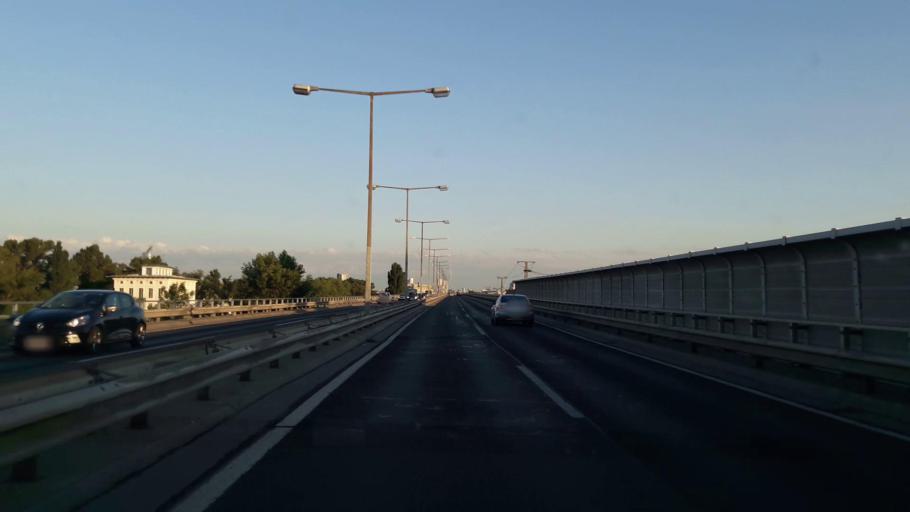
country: AT
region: Lower Austria
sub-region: Politischer Bezirk Korneuburg
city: Langenzersdorf
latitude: 48.2617
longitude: 16.3680
